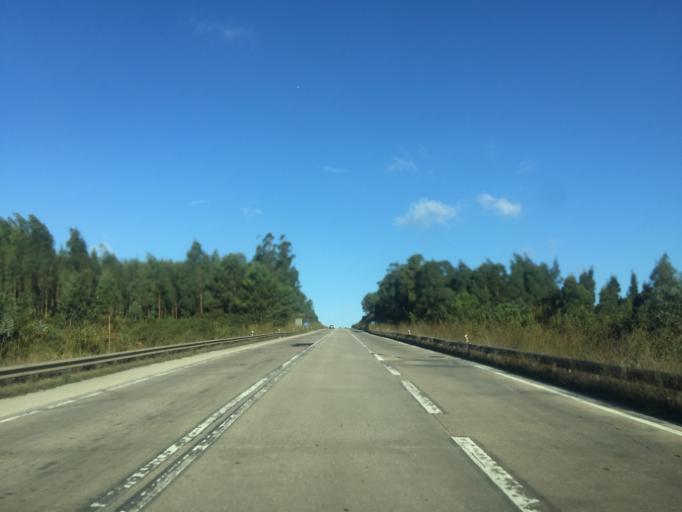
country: PT
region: Santarem
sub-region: Rio Maior
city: Rio Maior
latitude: 39.3409
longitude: -8.9682
